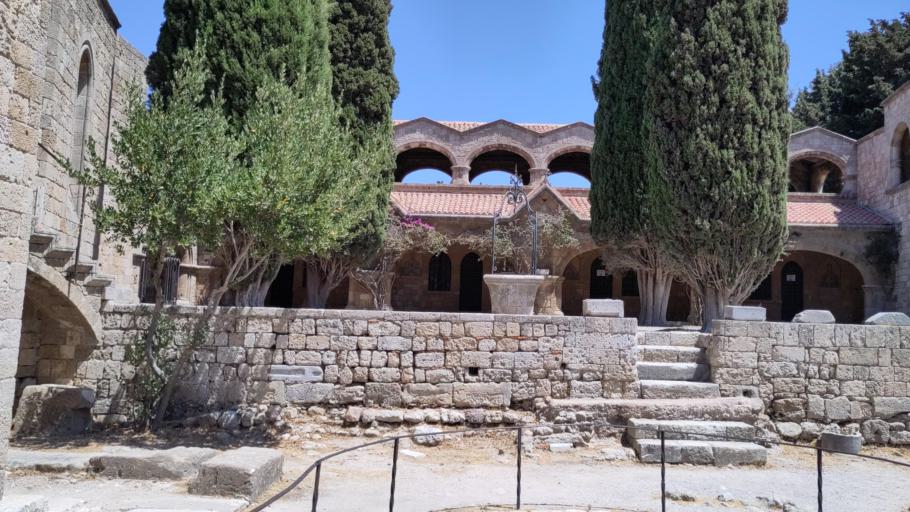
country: GR
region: South Aegean
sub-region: Nomos Dodekanisou
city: Trianta
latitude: 36.3989
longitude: 28.1441
